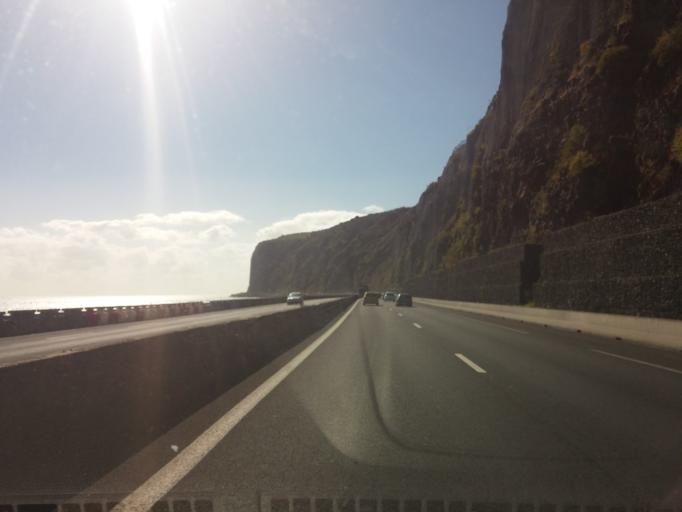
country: RE
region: Reunion
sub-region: Reunion
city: La Possession
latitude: -20.9107
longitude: 55.3547
